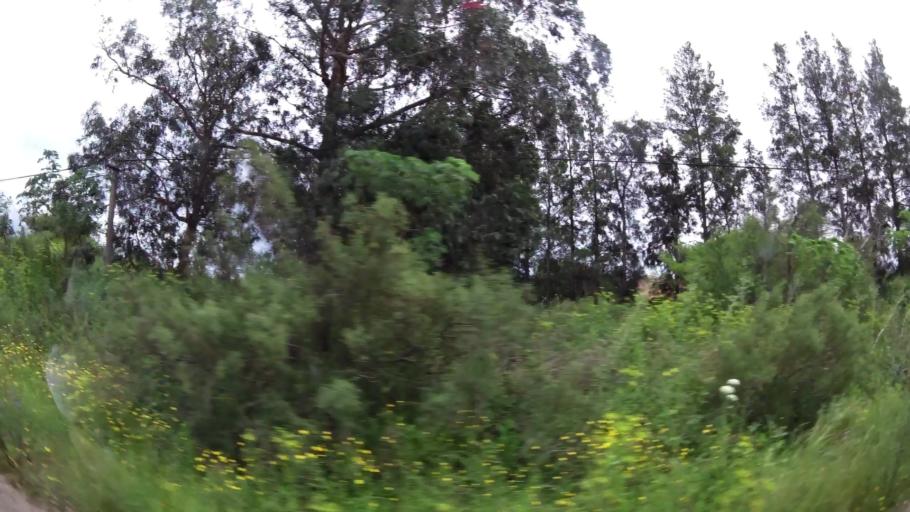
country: UY
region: Canelones
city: La Paz
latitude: -34.8013
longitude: -56.1568
